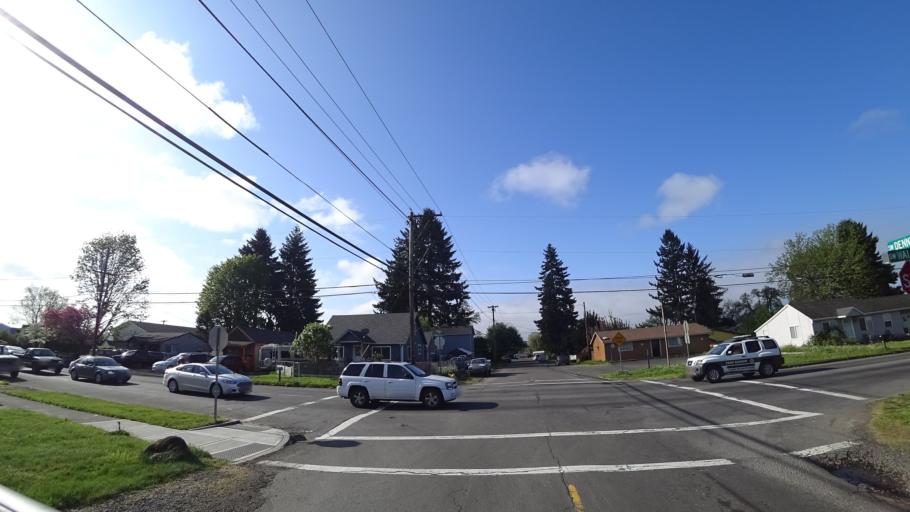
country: US
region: Oregon
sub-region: Washington County
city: Hillsboro
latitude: 45.5178
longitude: -122.9958
